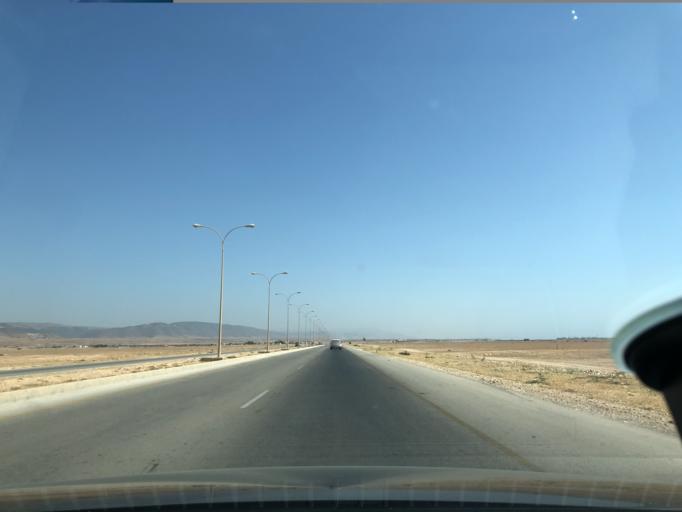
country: OM
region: Zufar
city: Salalah
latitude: 17.0513
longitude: 54.2582
